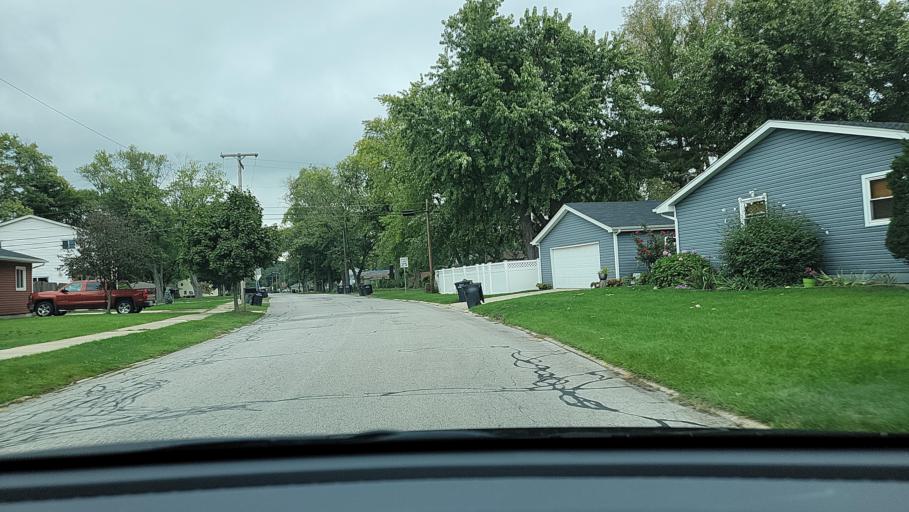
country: US
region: Indiana
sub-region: Porter County
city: Portage
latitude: 41.5611
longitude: -87.2060
